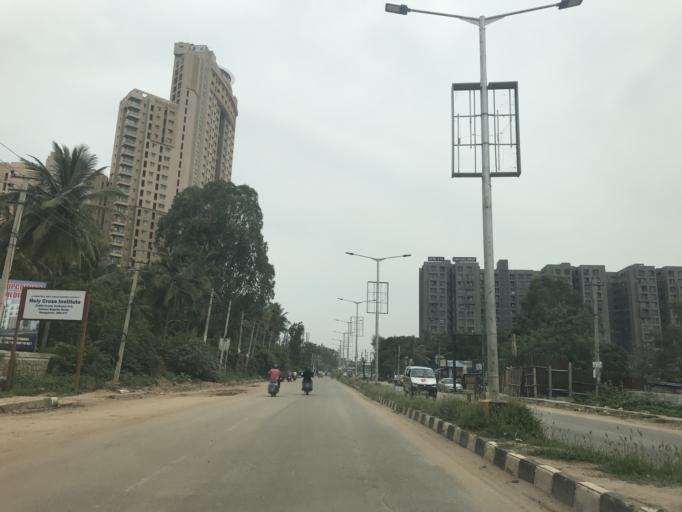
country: IN
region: Karnataka
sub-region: Bangalore Urban
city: Yelahanka
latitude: 13.0684
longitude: 77.6517
